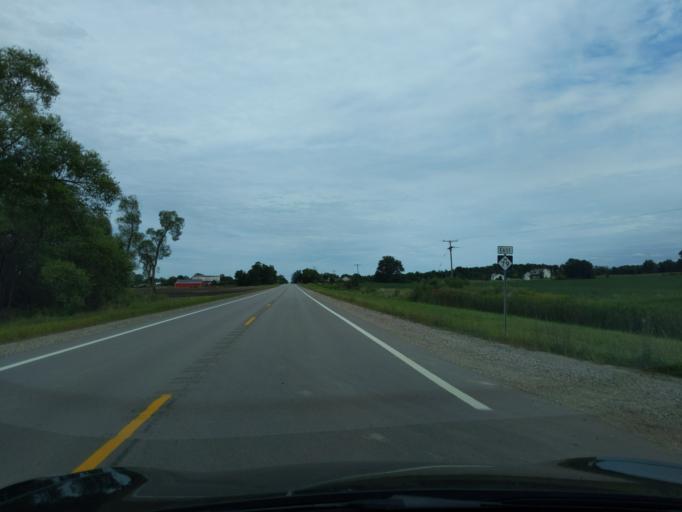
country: US
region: Michigan
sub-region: Barry County
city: Nashville
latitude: 42.5672
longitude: -84.9945
